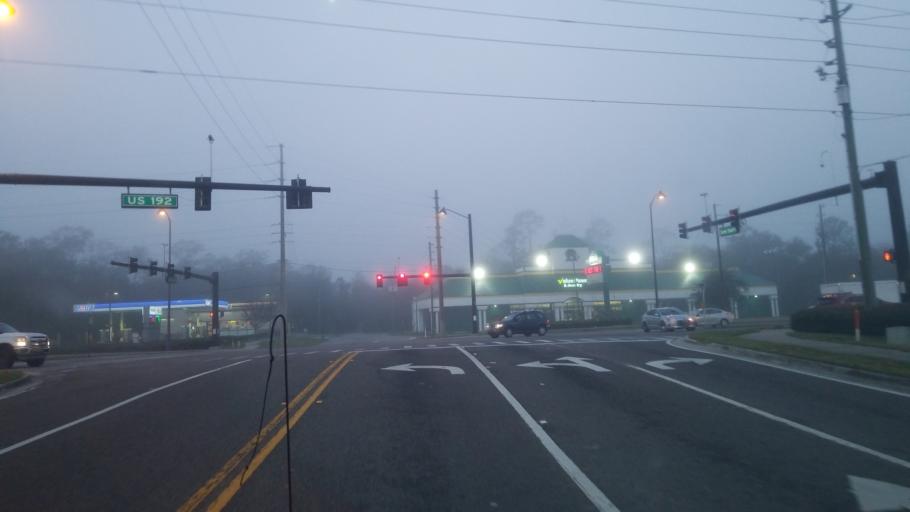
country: US
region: Florida
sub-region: Osceola County
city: Kissimmee
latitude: 28.3258
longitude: -81.4702
